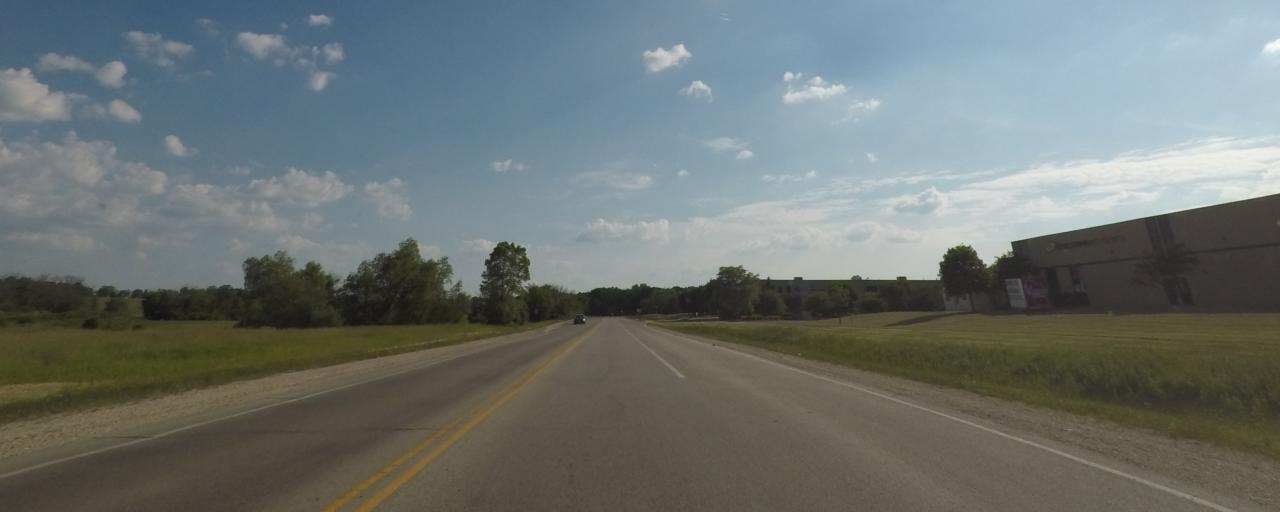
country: US
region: Wisconsin
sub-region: Waukesha County
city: New Berlin
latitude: 42.9404
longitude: -88.1101
